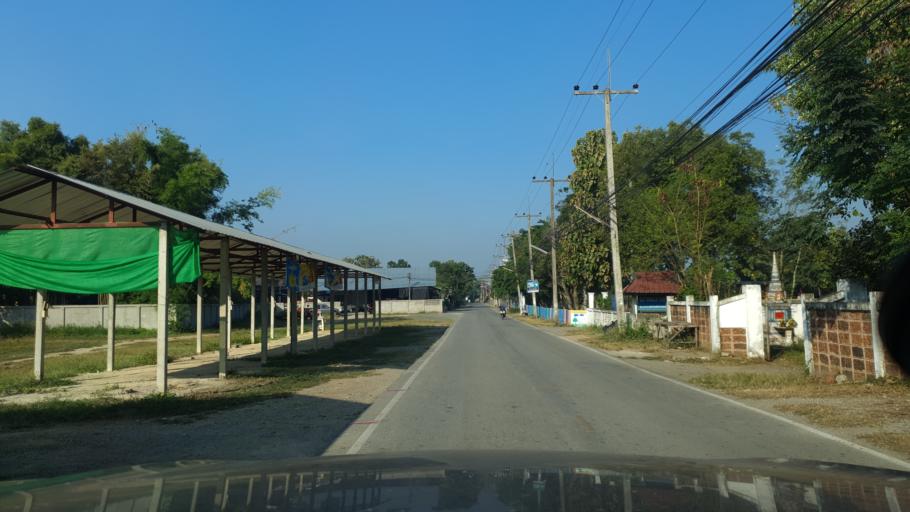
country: TH
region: Chiang Mai
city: San Kamphaeng
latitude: 18.7203
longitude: 99.1078
